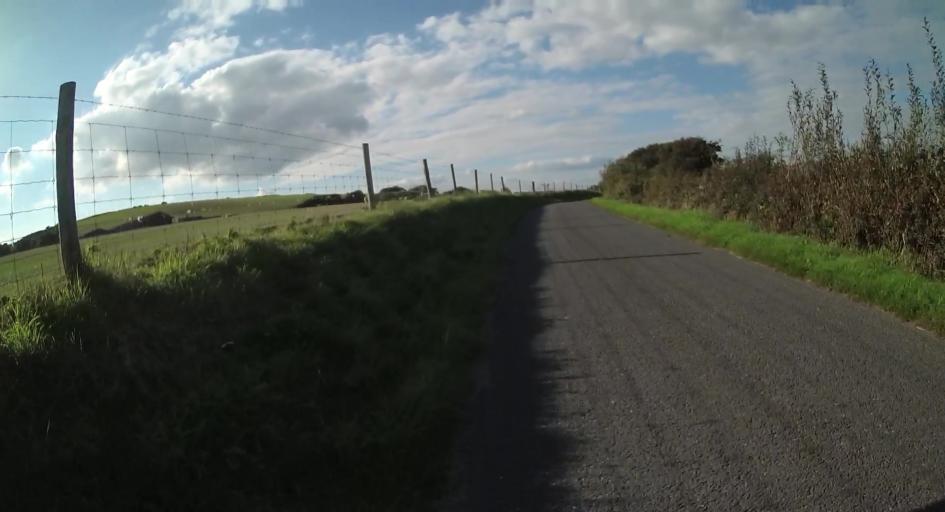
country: GB
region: England
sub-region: Isle of Wight
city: Chale
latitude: 50.6470
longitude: -1.2987
